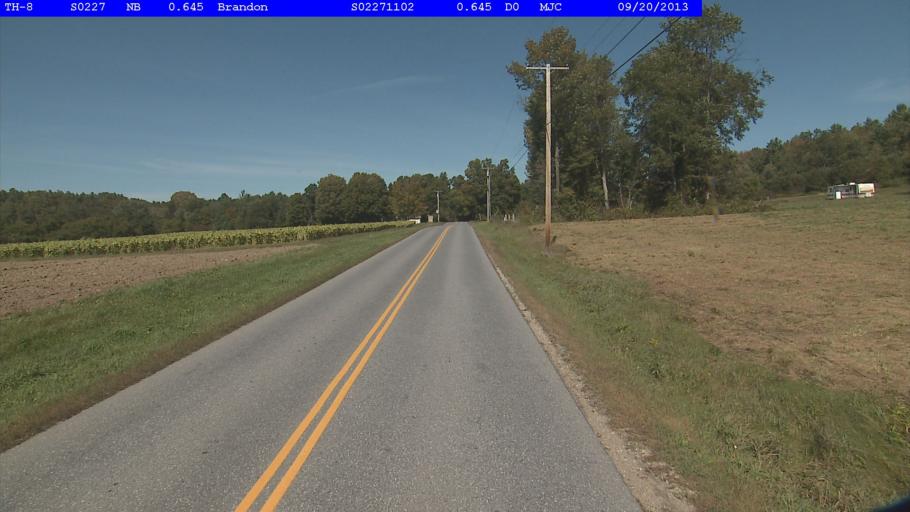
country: US
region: Vermont
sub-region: Rutland County
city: Brandon
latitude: 43.7837
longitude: -73.0531
